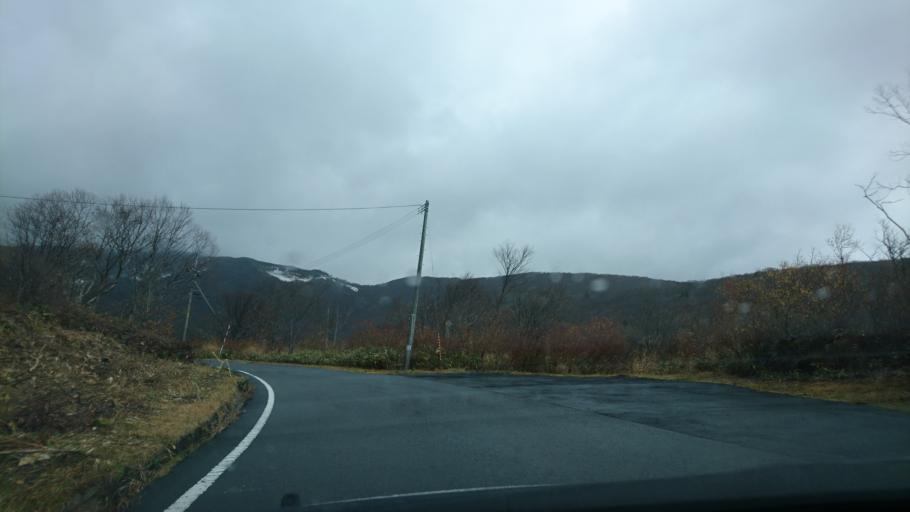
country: JP
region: Iwate
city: Ichinoseki
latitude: 38.9412
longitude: 140.8207
